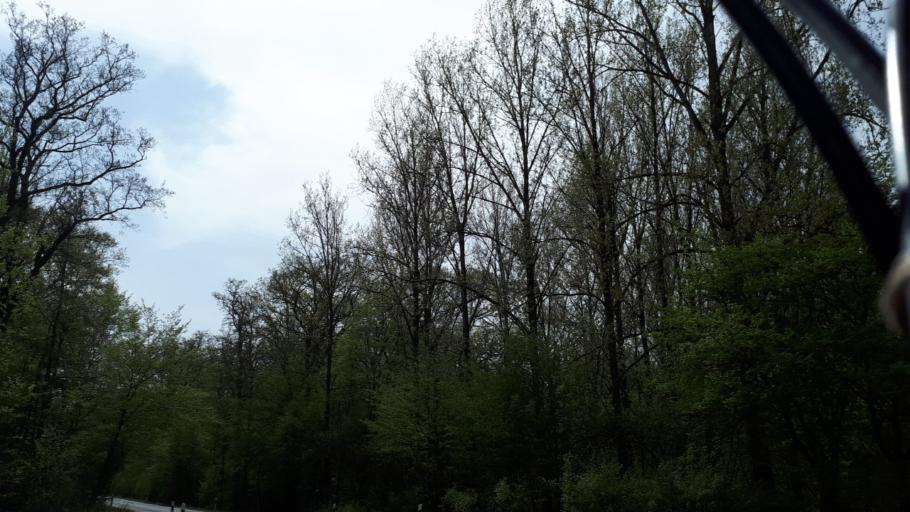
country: LU
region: Luxembourg
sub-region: Canton de Luxembourg
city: Bertrange
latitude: 49.5918
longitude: 6.0588
